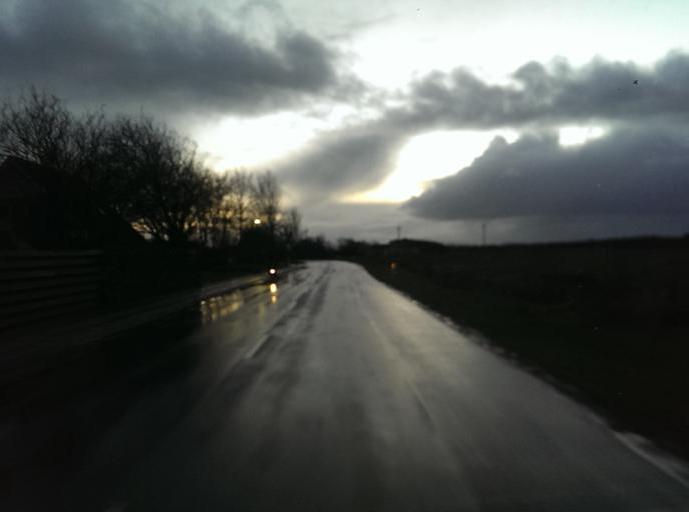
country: DK
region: South Denmark
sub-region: Esbjerg Kommune
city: Bramming
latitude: 55.4620
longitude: 8.6949
